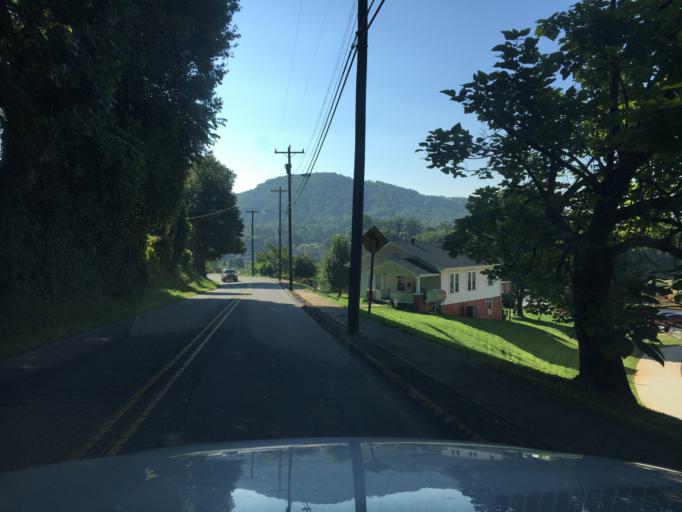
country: US
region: North Carolina
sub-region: McDowell County
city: Marion
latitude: 35.6822
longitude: -82.0173
